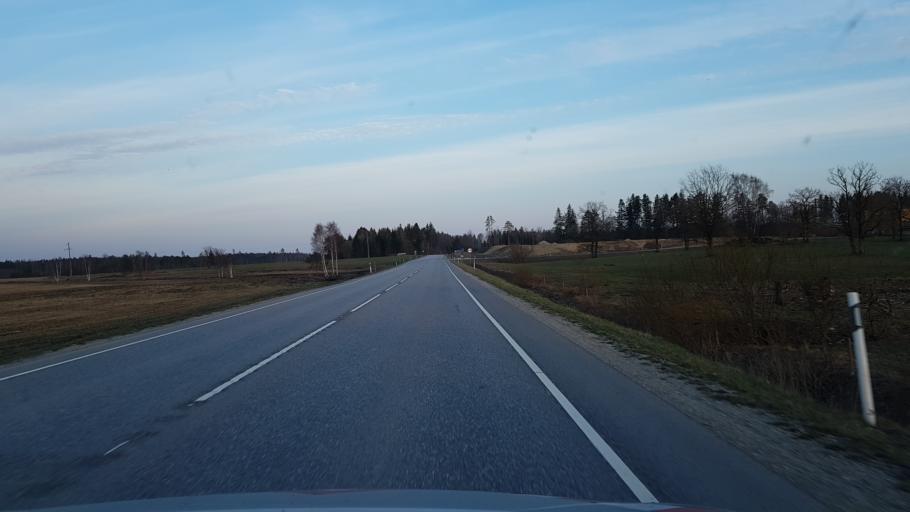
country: EE
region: Laeaene-Virumaa
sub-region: Someru vald
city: Someru
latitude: 59.3473
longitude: 26.4056
